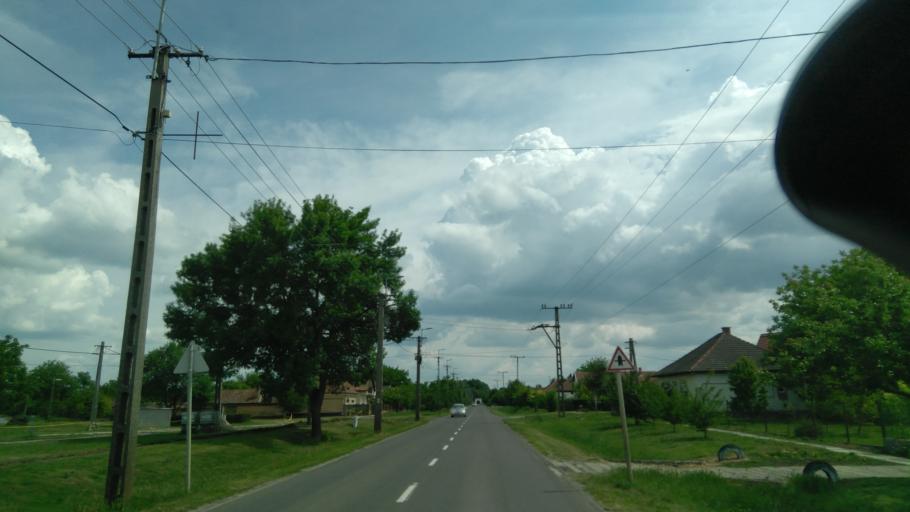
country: HU
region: Bekes
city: Mezohegyes
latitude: 46.3258
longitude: 20.8128
